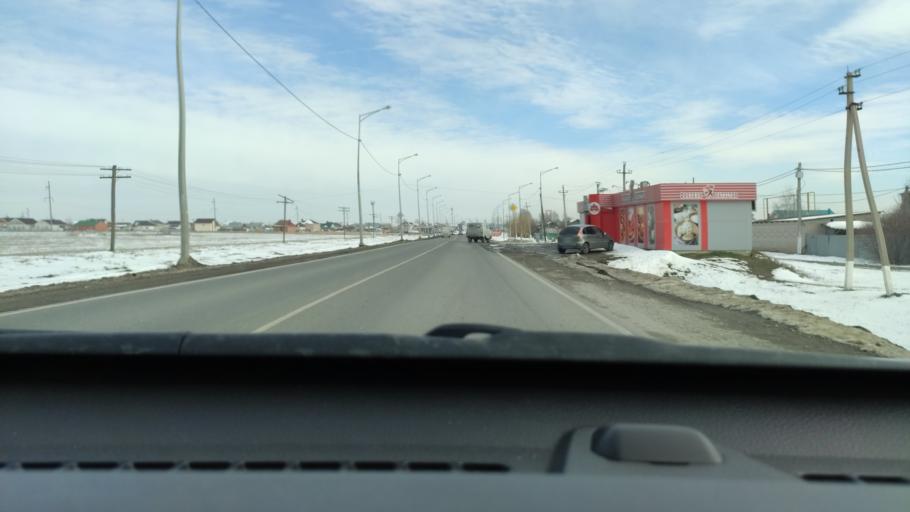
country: RU
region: Samara
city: Zhigulevsk
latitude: 53.5449
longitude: 49.5179
